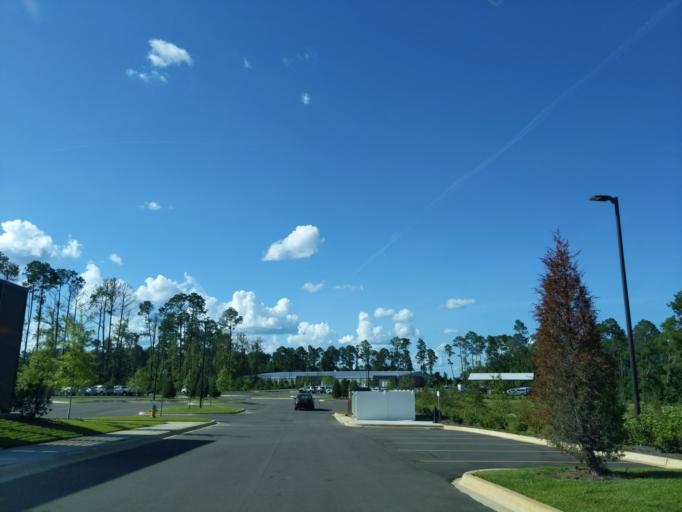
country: US
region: Florida
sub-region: Leon County
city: Tallahassee
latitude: 30.4074
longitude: -84.2448
